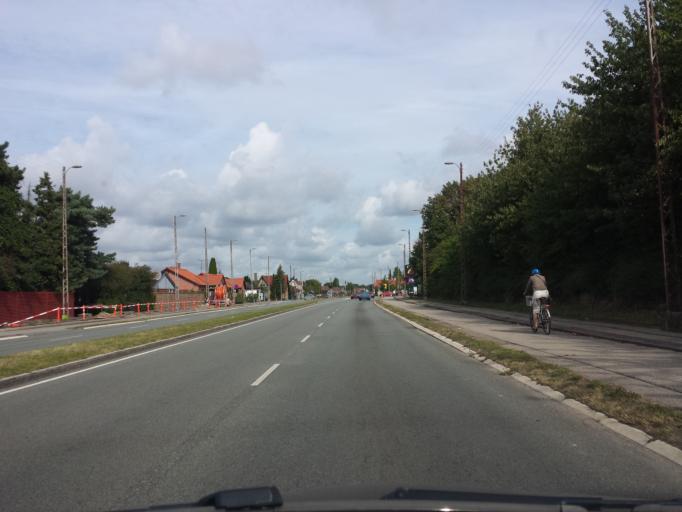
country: DK
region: Capital Region
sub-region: Rodovre Kommune
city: Rodovre
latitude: 55.6843
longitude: 12.4518
